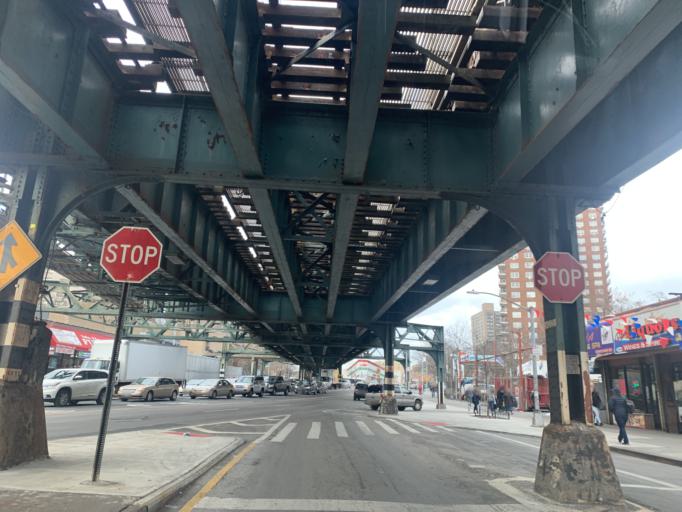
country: US
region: New York
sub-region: Bronx
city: The Bronx
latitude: 40.8585
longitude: -73.8675
